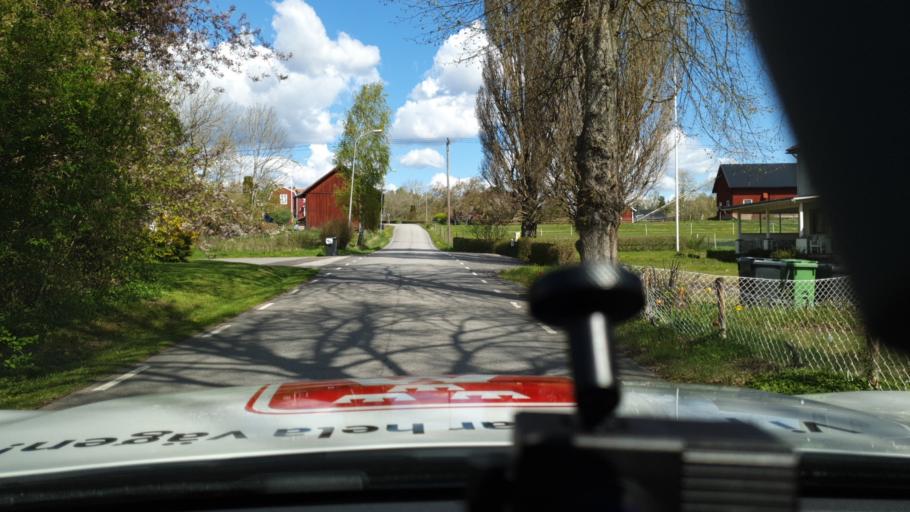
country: SE
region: Kalmar
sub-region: Vasterviks Kommun
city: Ankarsrum
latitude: 57.7795
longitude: 16.1514
